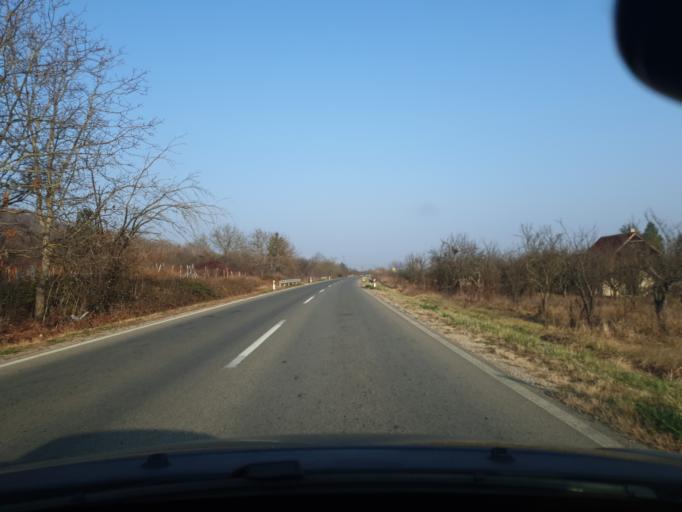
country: RS
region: Central Serbia
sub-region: Jablanicki Okrug
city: Leskovac
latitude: 42.9670
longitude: 21.9782
